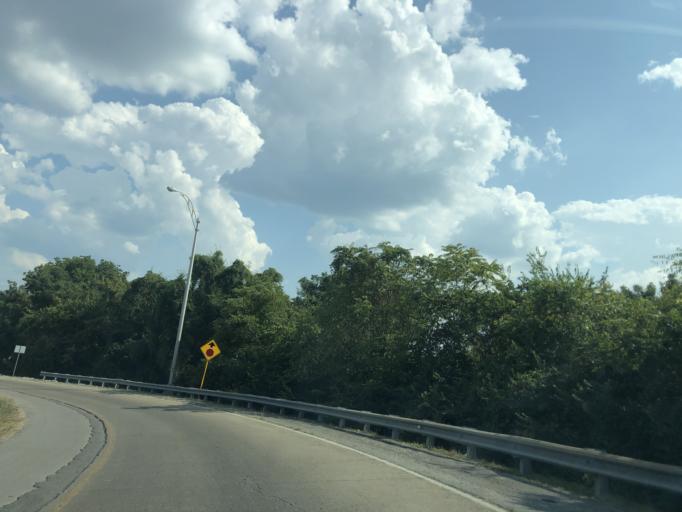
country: US
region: Tennessee
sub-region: Davidson County
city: Oak Hill
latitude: 36.1094
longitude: -86.7745
